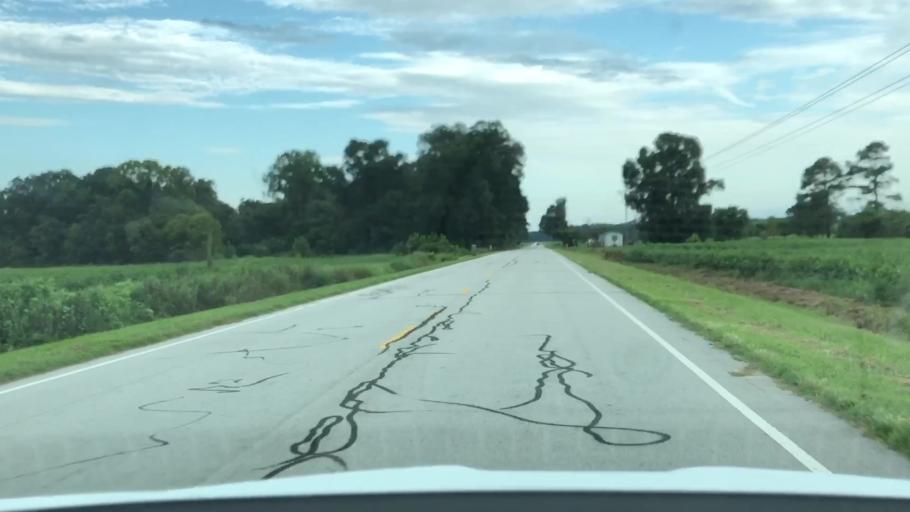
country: US
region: North Carolina
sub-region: Jones County
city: Trenton
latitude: 35.1018
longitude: -77.4914
